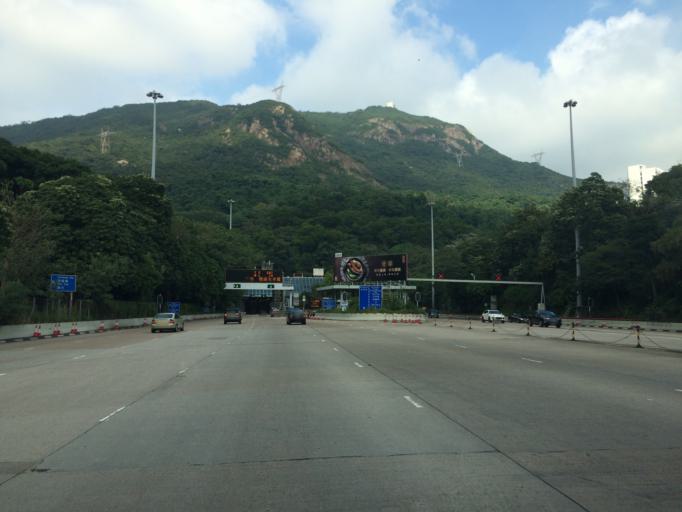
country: HK
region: Wanchai
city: Wan Chai
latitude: 22.2518
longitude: 114.1781
